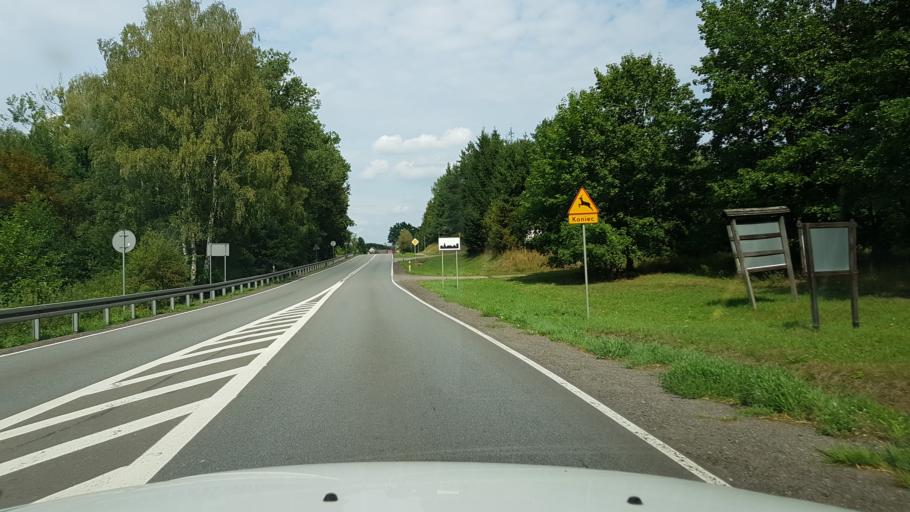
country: PL
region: West Pomeranian Voivodeship
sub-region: Powiat walecki
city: Walcz
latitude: 53.2956
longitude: 16.5266
